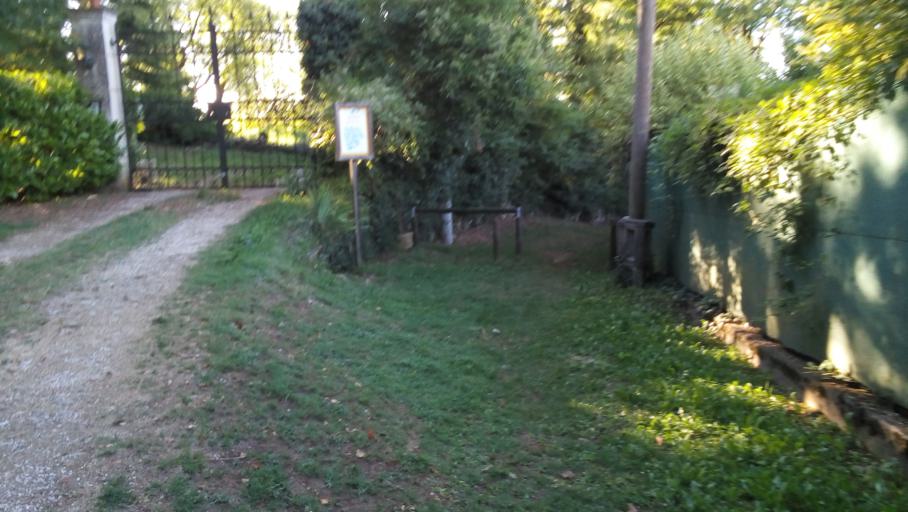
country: IT
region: Veneto
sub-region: Provincia di Vicenza
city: Creazzo
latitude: 45.5375
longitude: 11.4614
